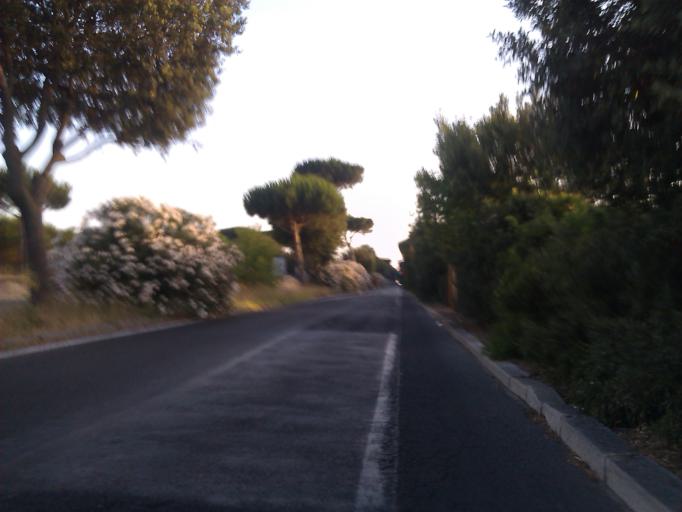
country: IT
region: Latium
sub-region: Citta metropolitana di Roma Capitale
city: Acilia-Castel Fusano-Ostia Antica
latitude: 41.7248
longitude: 12.3303
